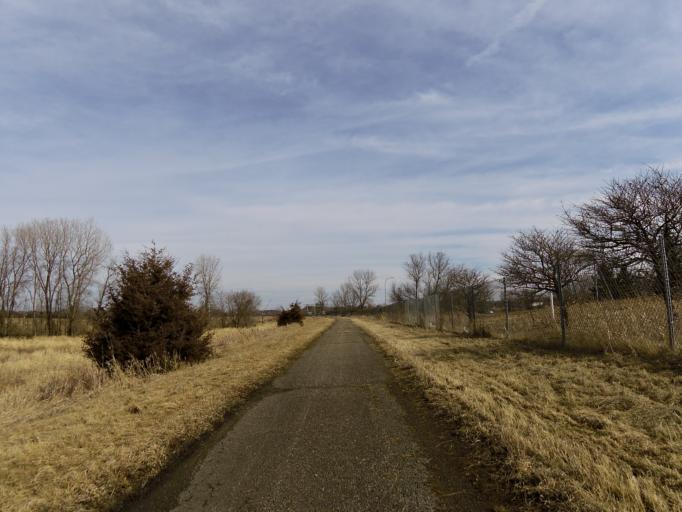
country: US
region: Minnesota
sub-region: Washington County
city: Lake Elmo
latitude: 44.9495
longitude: -92.8604
